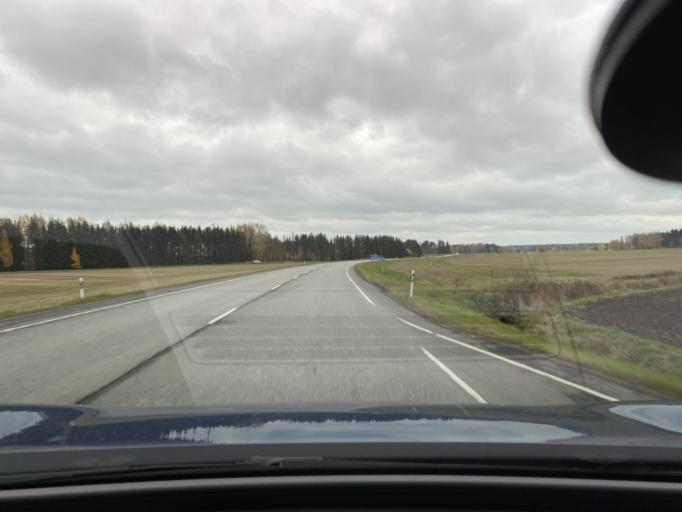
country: FI
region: Satakunta
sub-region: Rauma
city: Kiukainen
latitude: 61.1927
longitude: 22.0591
